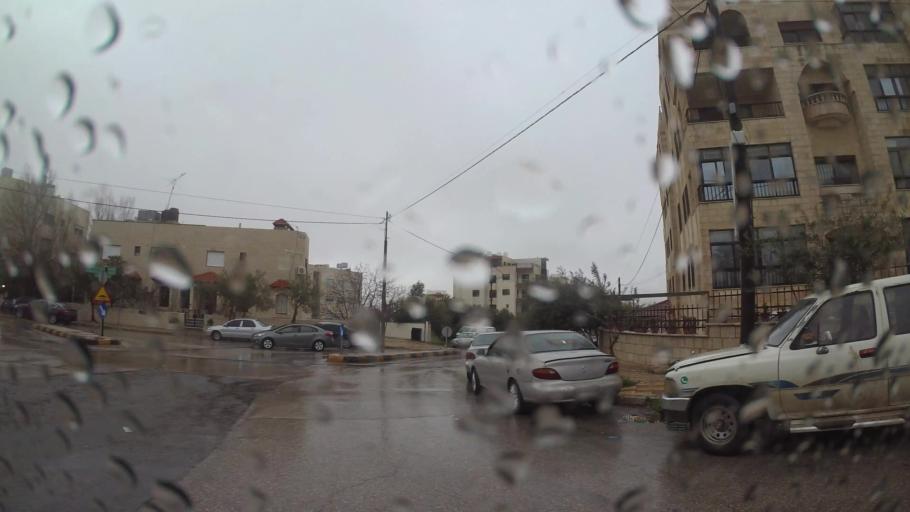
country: JO
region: Amman
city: Al Jubayhah
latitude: 32.0296
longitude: 35.8529
